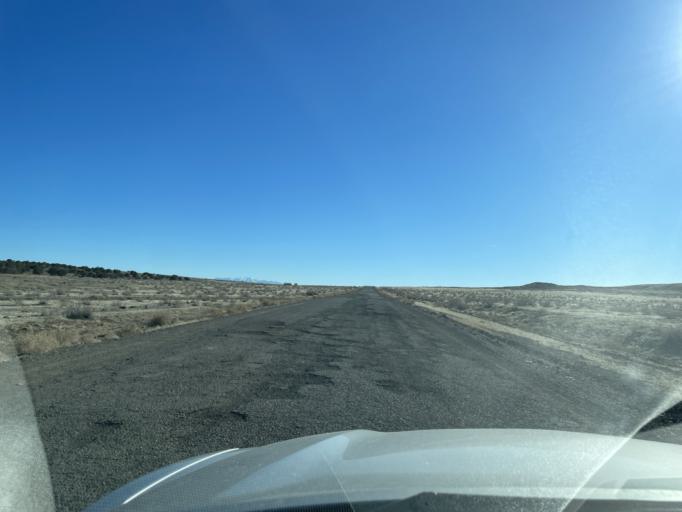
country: US
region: Colorado
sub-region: Mesa County
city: Loma
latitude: 39.1853
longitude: -109.1281
